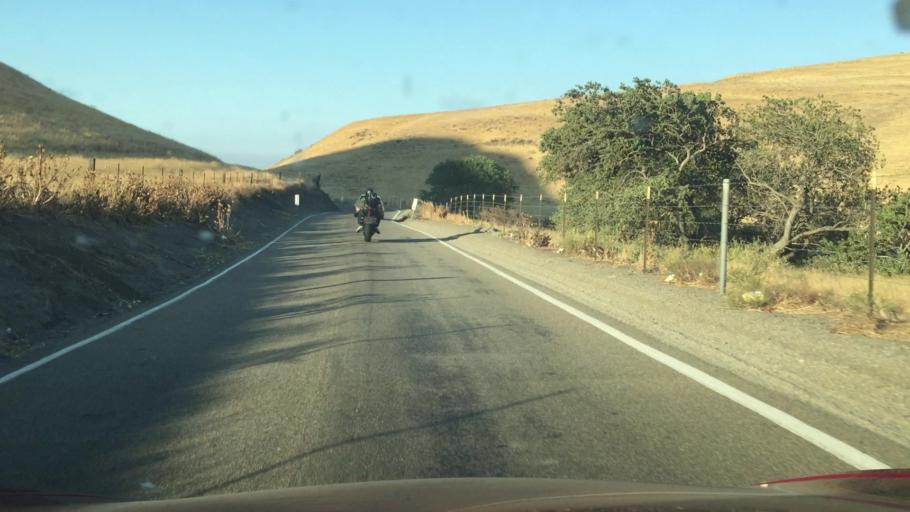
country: US
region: California
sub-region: San Joaquin County
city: Mountain House
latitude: 37.6872
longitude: -121.5971
